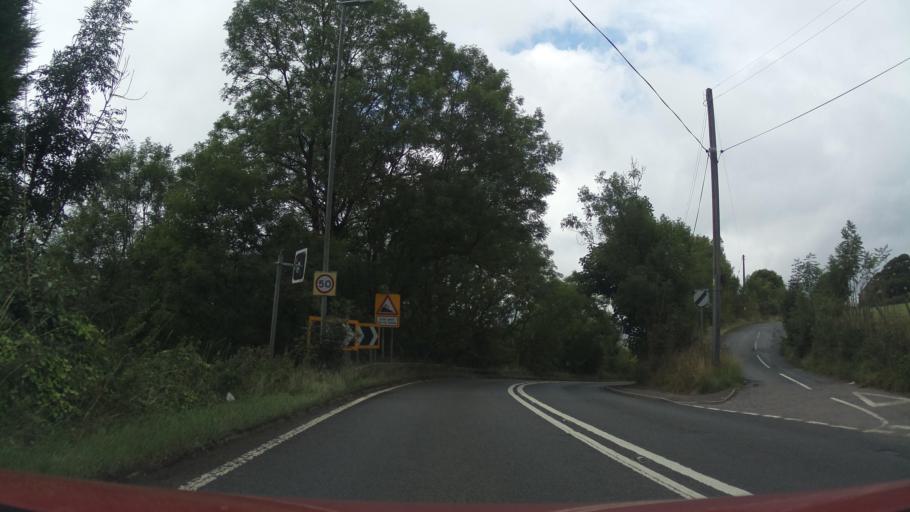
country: GB
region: England
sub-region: Kirklees
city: Kirkburton
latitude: 53.5734
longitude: -1.7301
